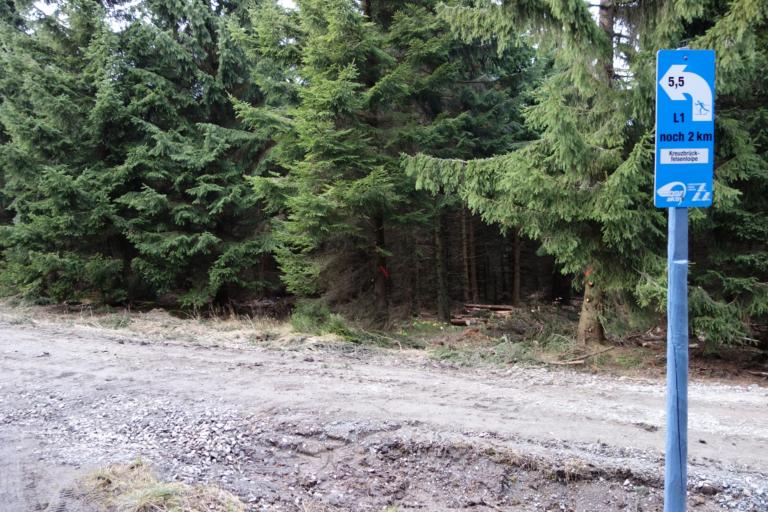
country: DE
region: Saxony
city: Kurort Oberwiesenthal
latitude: 50.4427
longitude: 12.9775
